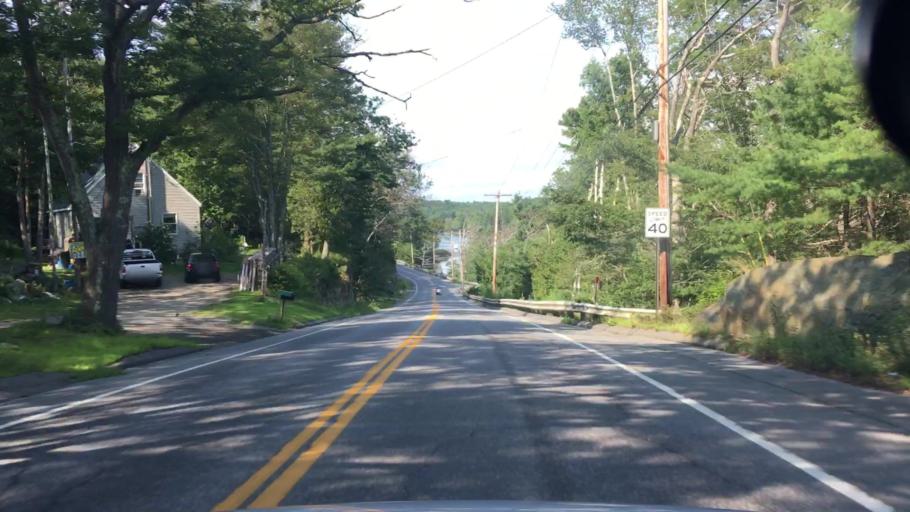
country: US
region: Maine
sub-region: Cumberland County
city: Harpswell Center
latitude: 43.7973
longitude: -69.9354
